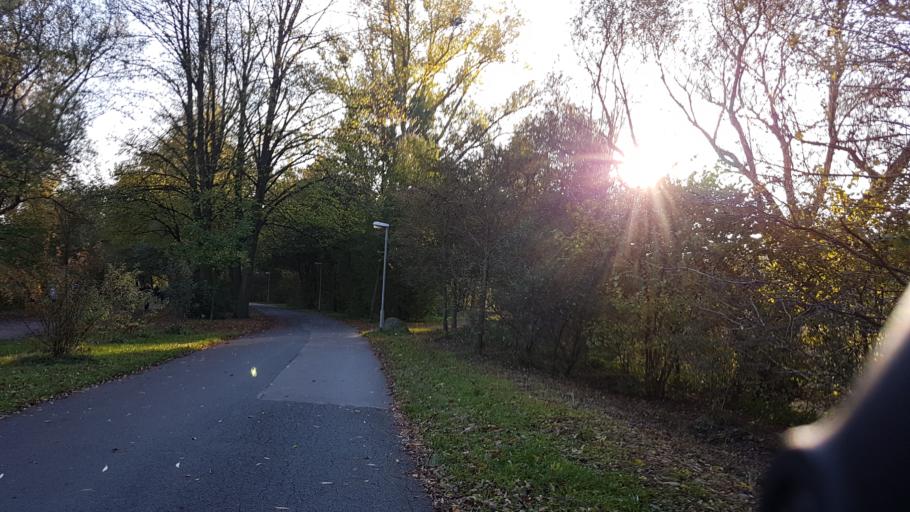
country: DE
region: Lower Saxony
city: Hannover
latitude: 52.3485
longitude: 9.7448
